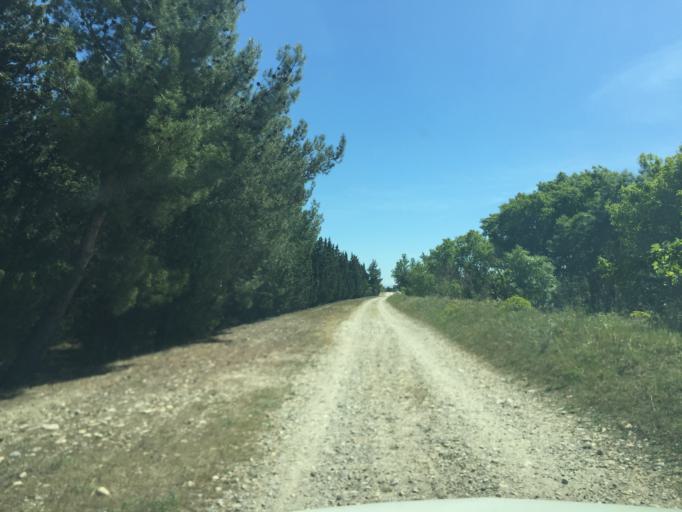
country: FR
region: Languedoc-Roussillon
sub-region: Departement du Gard
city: Roquemaure
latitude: 44.0502
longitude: 4.7968
